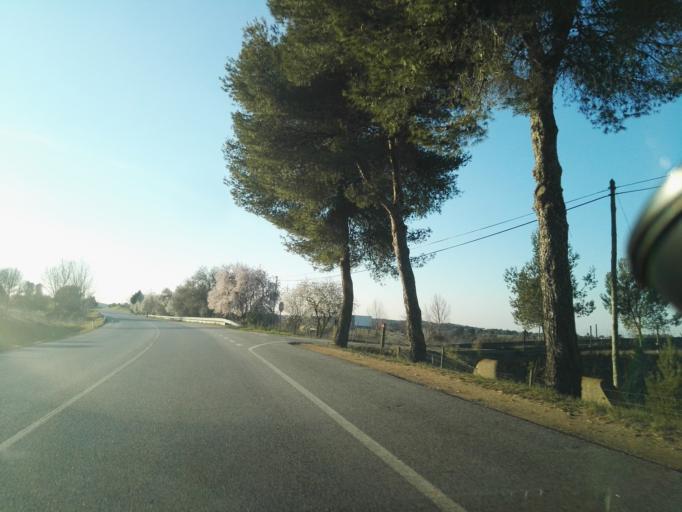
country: PT
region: Evora
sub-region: Montemor-O-Novo
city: Montemor-o-Novo
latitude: 38.6459
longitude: -8.1552
